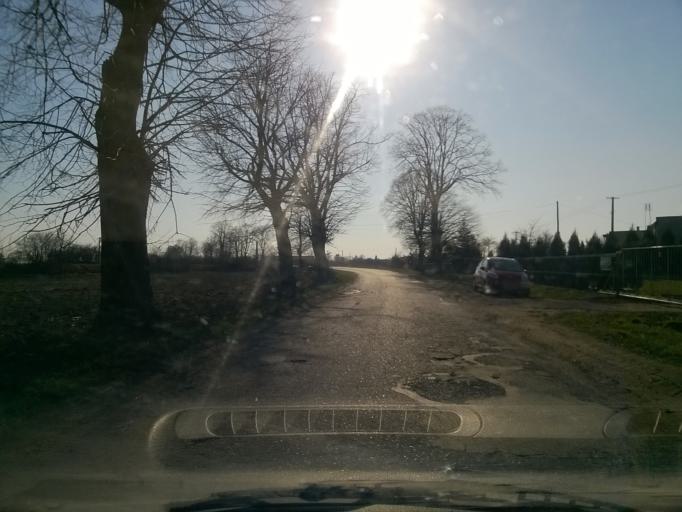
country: PL
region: Greater Poland Voivodeship
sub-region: Powiat wagrowiecki
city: Golancz
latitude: 52.9510
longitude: 17.3192
